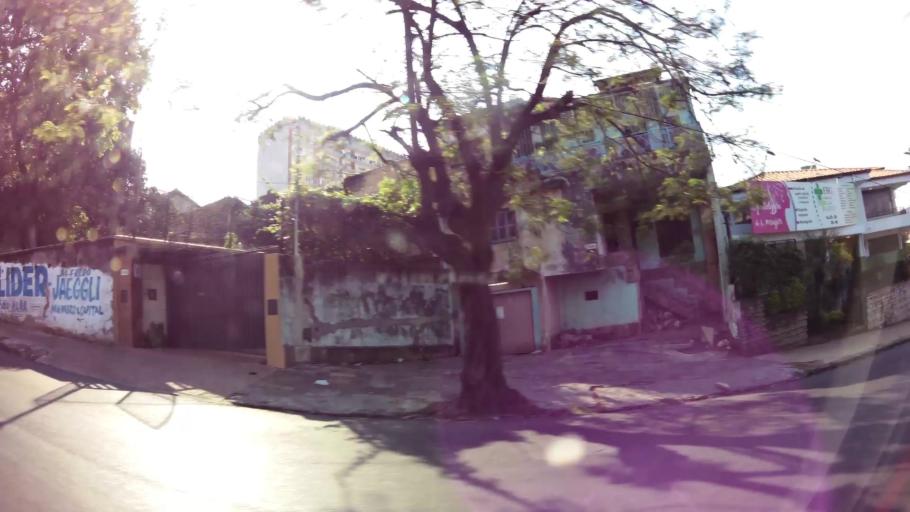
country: PY
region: Asuncion
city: Asuncion
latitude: -25.2952
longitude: -57.6235
